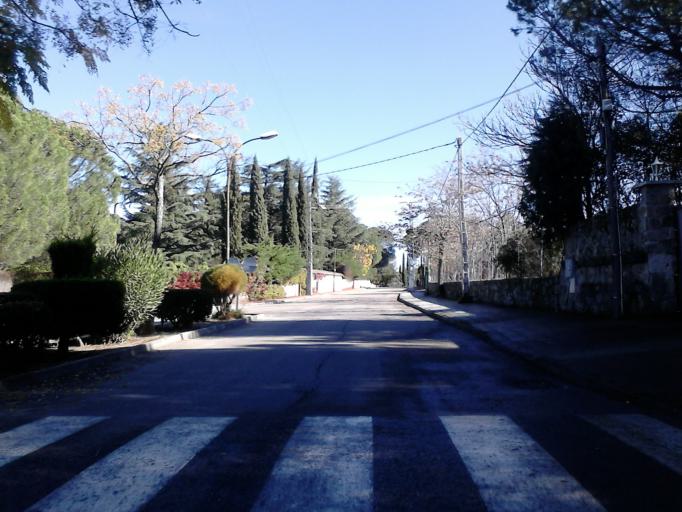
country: ES
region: Madrid
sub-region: Provincia de Madrid
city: Galapagar
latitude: 40.5742
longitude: -3.9965
